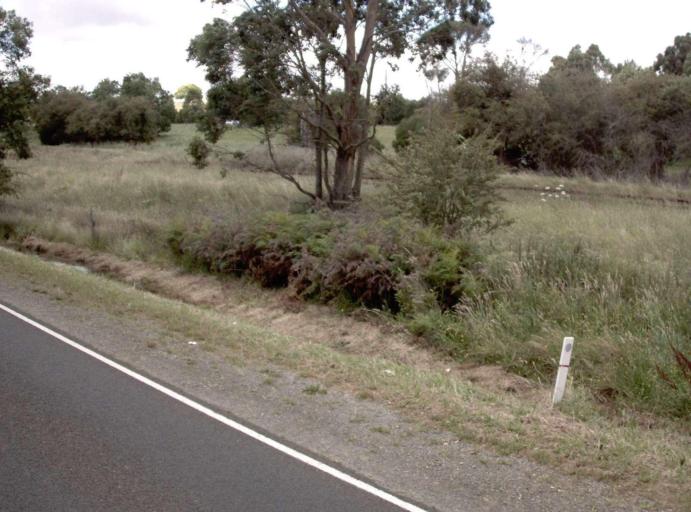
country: AU
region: Victoria
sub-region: Baw Baw
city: Warragul
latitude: -38.1678
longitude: 145.9565
